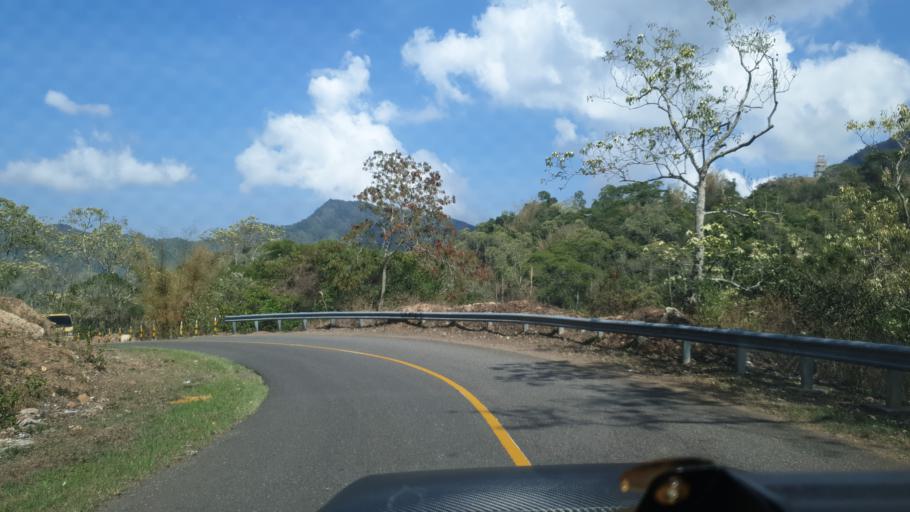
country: ID
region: East Nusa Tenggara
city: Nduaria
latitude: -8.6984
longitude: 121.8137
